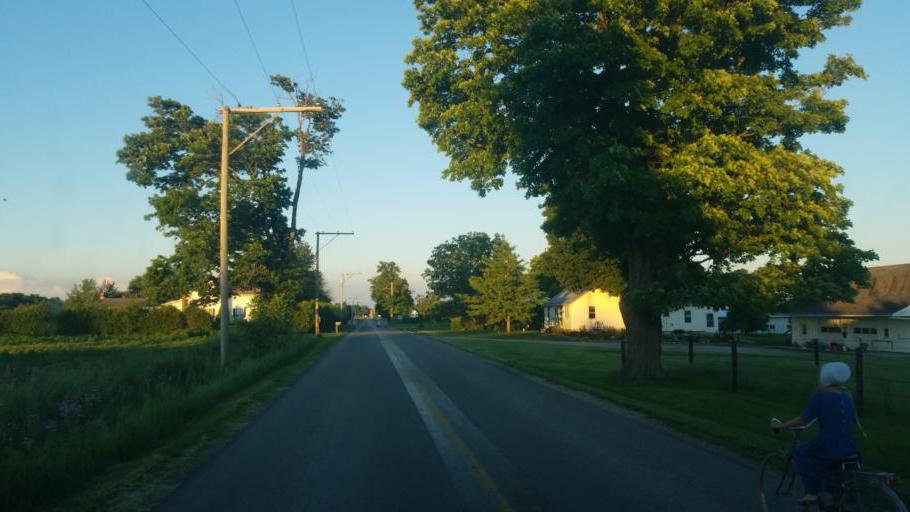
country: US
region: Indiana
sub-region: Elkhart County
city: Nappanee
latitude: 41.4266
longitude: -86.0148
